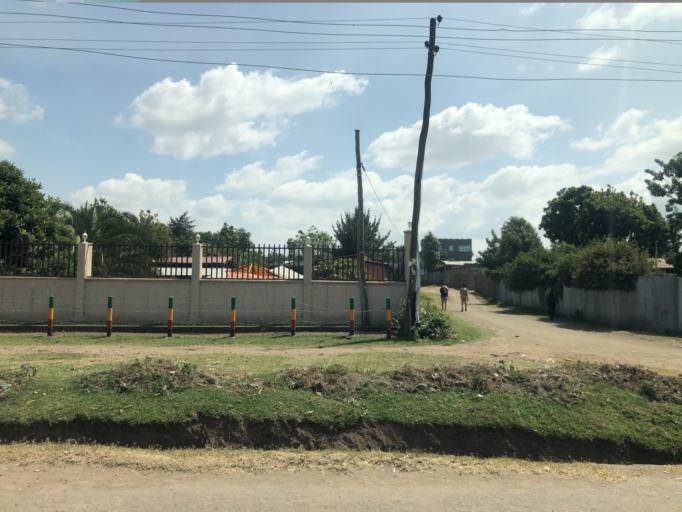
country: ET
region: Oromiya
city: Shashemene
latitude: 7.2080
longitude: 38.6128
